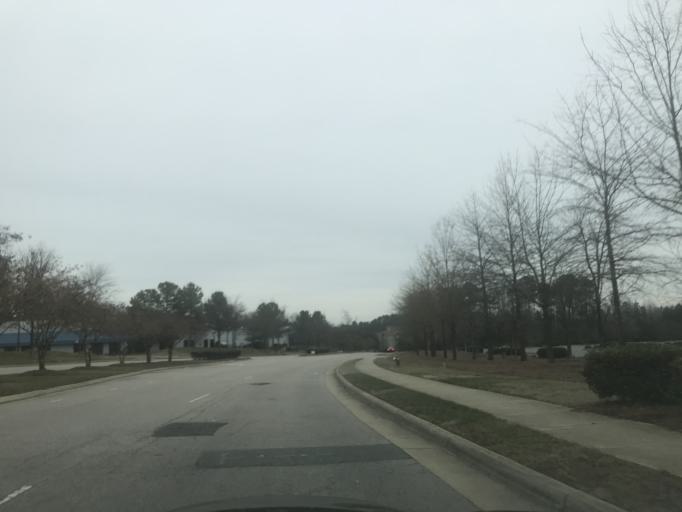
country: US
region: North Carolina
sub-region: Wake County
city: Raleigh
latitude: 35.8736
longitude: -78.5896
